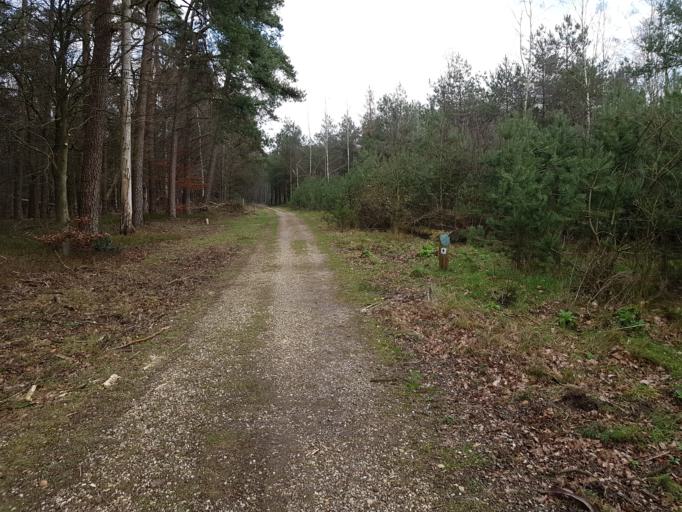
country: NL
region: Gelderland
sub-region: Gemeente Apeldoorn
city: Apeldoorn
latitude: 52.2227
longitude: 5.8841
